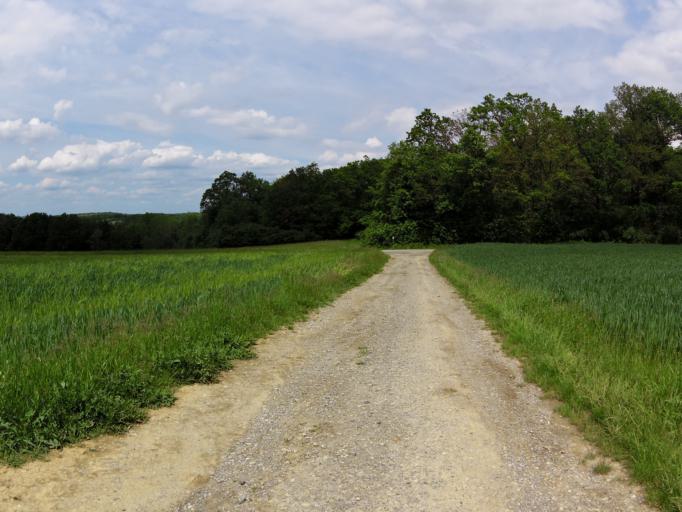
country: DE
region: Bavaria
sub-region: Regierungsbezirk Unterfranken
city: Sommerhausen
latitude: 49.7176
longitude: 10.0283
